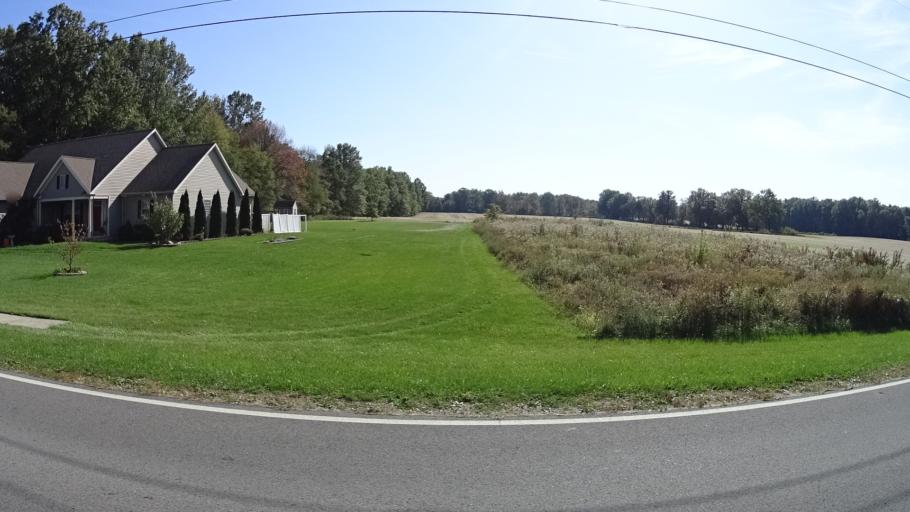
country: US
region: Ohio
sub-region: Lorain County
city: Vermilion-on-the-Lake
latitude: 41.4024
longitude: -82.3199
